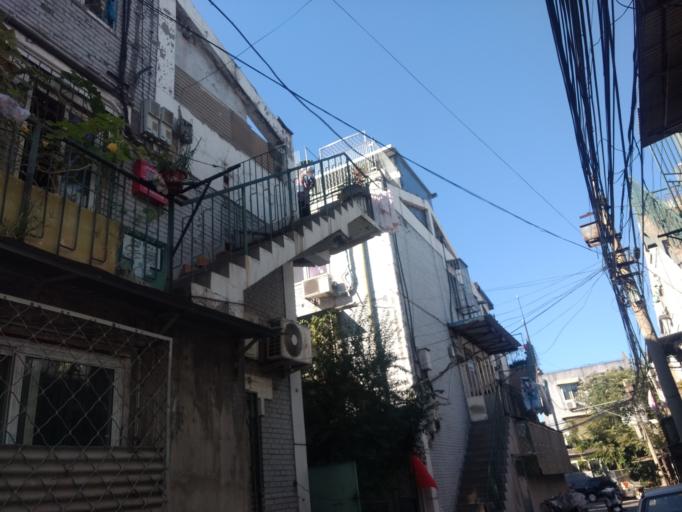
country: CN
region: Beijing
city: Beijing
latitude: 39.8928
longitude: 116.3819
